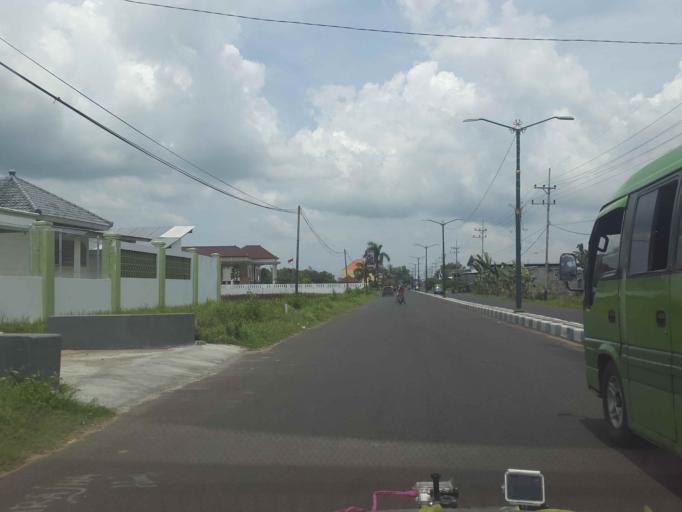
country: ID
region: East Java
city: Sumenep
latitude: -7.0356
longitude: 113.8501
